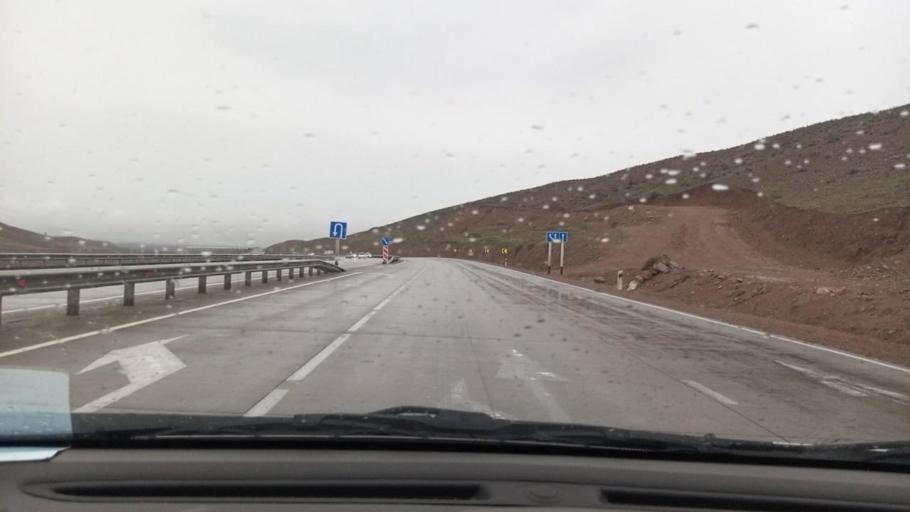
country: UZ
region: Namangan
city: Pop Shahri
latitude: 40.9319
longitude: 70.7021
